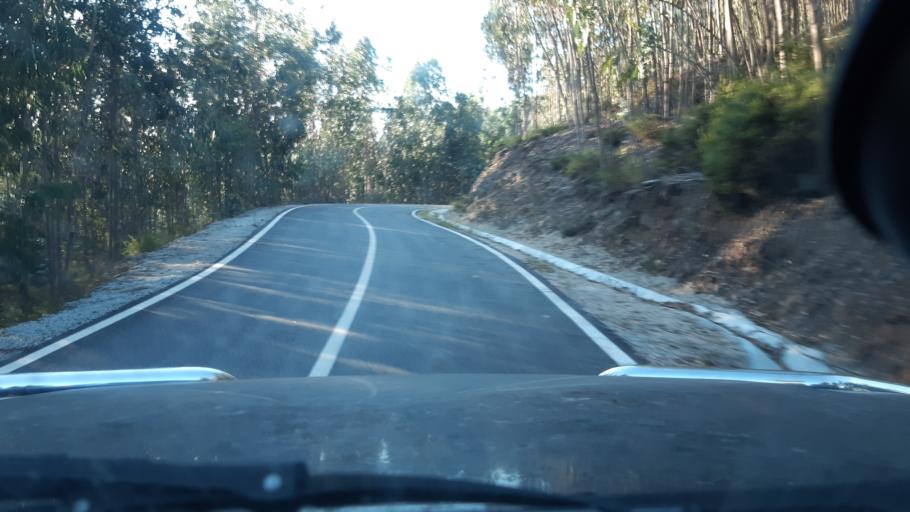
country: PT
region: Viseu
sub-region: Mortagua
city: Mortagua
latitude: 40.5379
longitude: -8.2461
